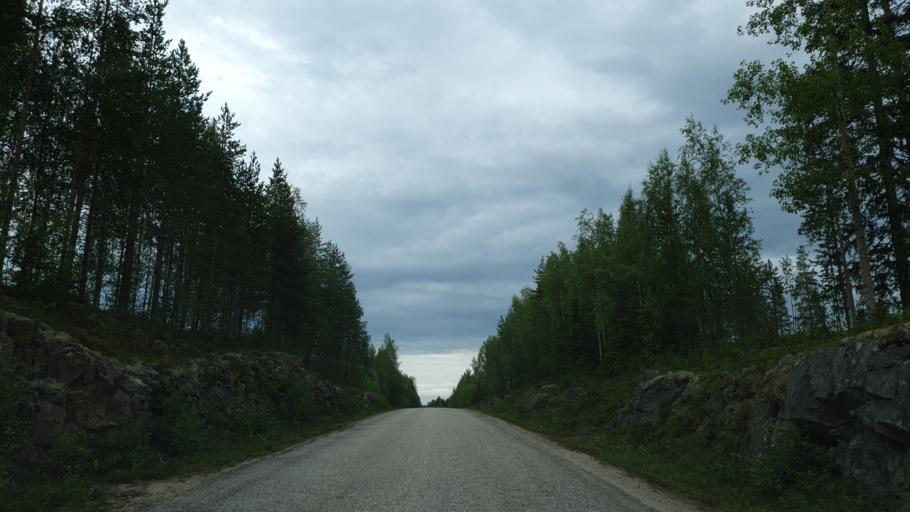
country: FI
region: Kainuu
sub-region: Kehys-Kainuu
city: Kuhmo
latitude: 64.3375
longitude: 29.3478
